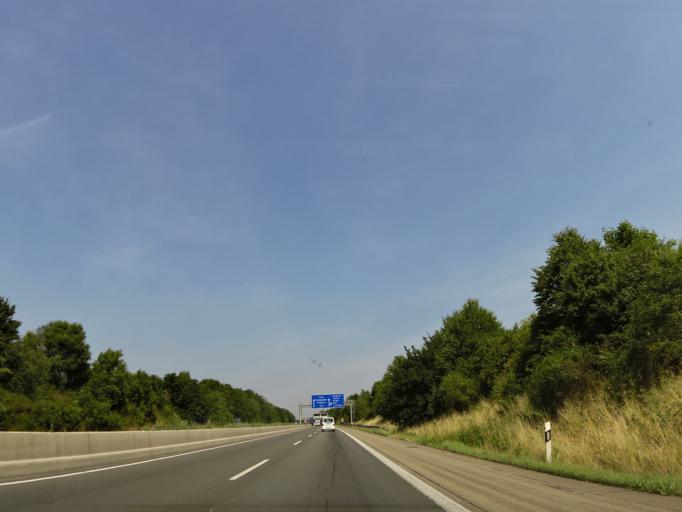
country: DE
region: North Rhine-Westphalia
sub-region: Regierungsbezirk Koln
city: Kerpen
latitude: 50.8793
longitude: 6.7059
